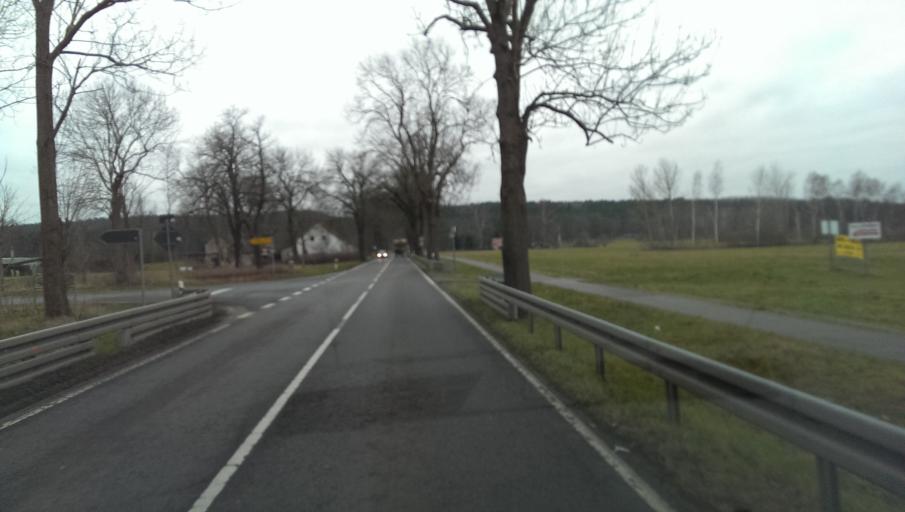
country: DE
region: Brandenburg
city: Zossen
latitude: 52.2241
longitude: 13.4889
